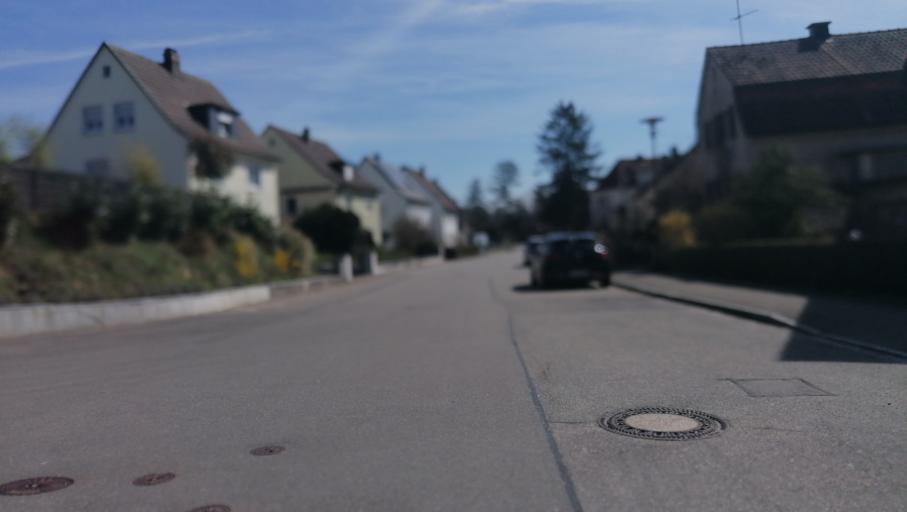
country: DE
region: Baden-Wuerttemberg
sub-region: Freiburg Region
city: Bad Sackingen
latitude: 47.5584
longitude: 7.9377
